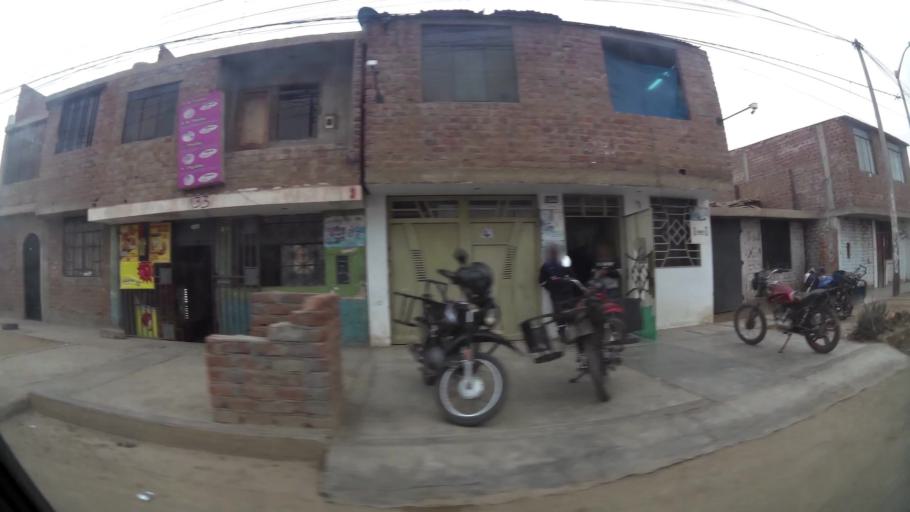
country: PE
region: La Libertad
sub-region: Provincia de Trujillo
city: El Porvenir
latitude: -8.0802
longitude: -79.0144
